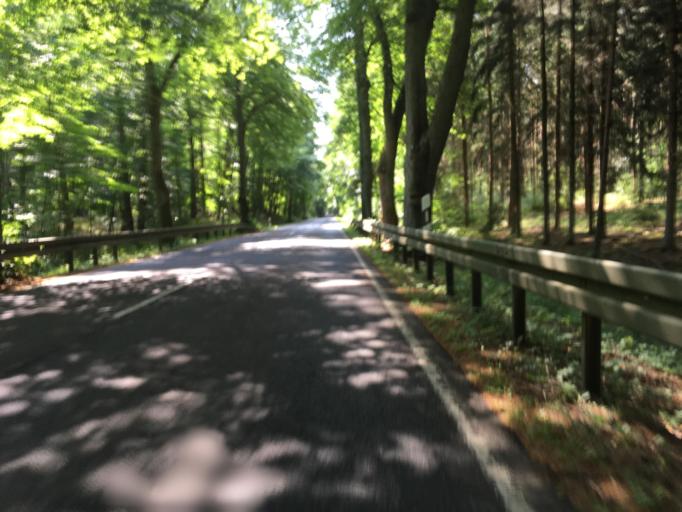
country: DE
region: Brandenburg
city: Friedrichswalde
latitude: 53.0840
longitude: 13.7190
